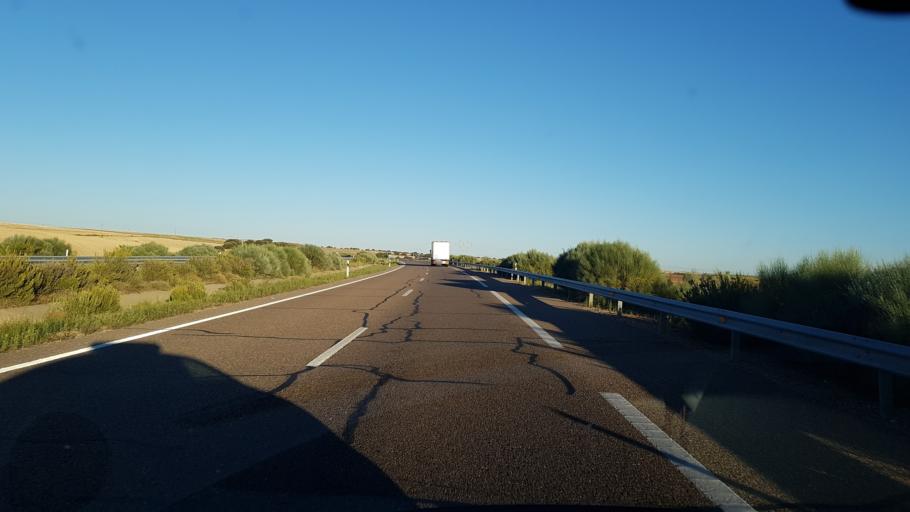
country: ES
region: Castille and Leon
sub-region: Provincia de Zamora
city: Matilla la Seca
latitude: 41.5690
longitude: -5.4934
